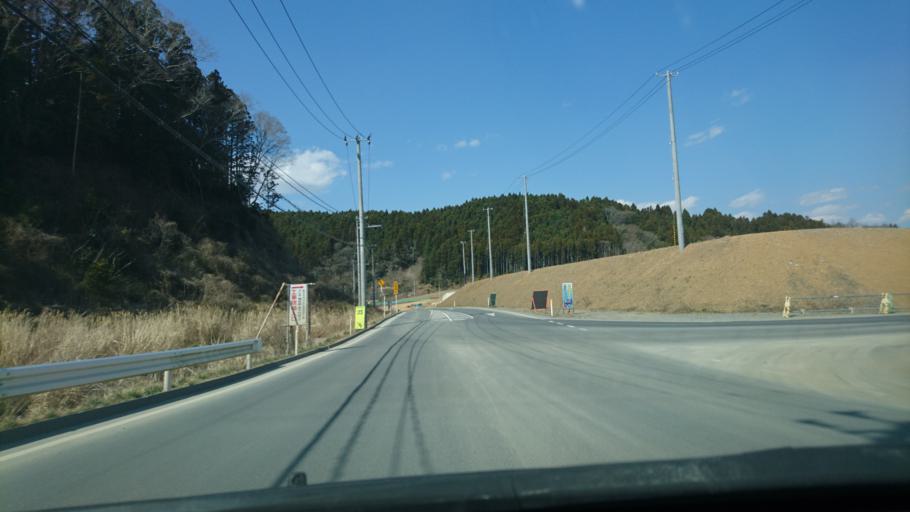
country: JP
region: Miyagi
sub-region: Oshika Gun
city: Onagawa Cho
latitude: 38.6448
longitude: 141.4375
